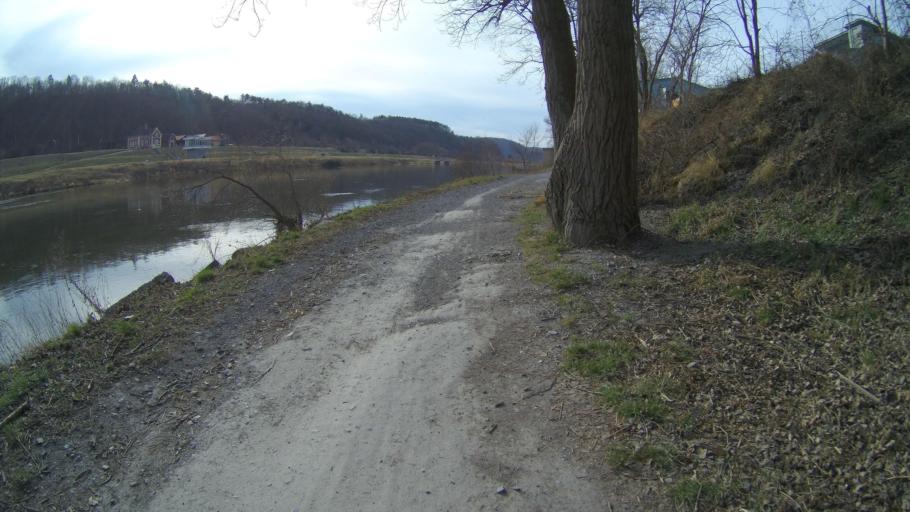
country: CZ
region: Central Bohemia
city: Roztoky
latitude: 50.1732
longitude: 14.3918
